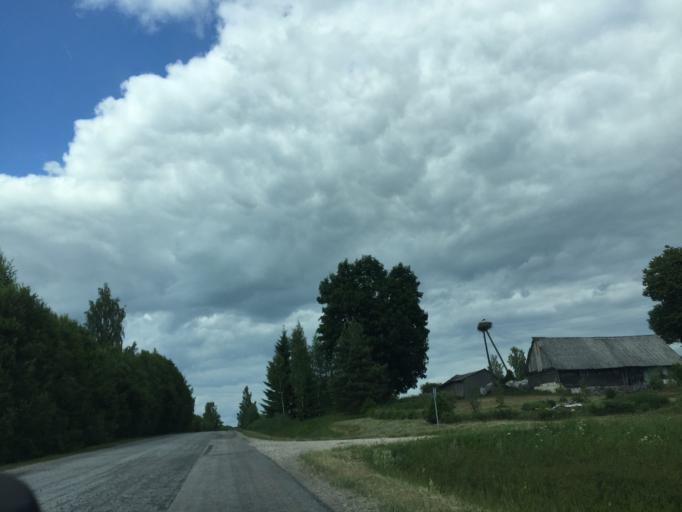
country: LV
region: Skriveri
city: Skriveri
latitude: 56.8187
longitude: 25.1191
